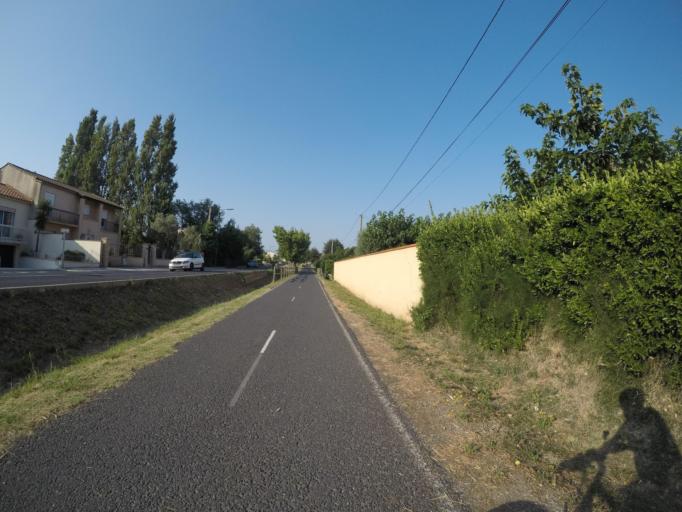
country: FR
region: Languedoc-Roussillon
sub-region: Departement des Pyrenees-Orientales
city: Canohes
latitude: 42.6565
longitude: 2.8338
